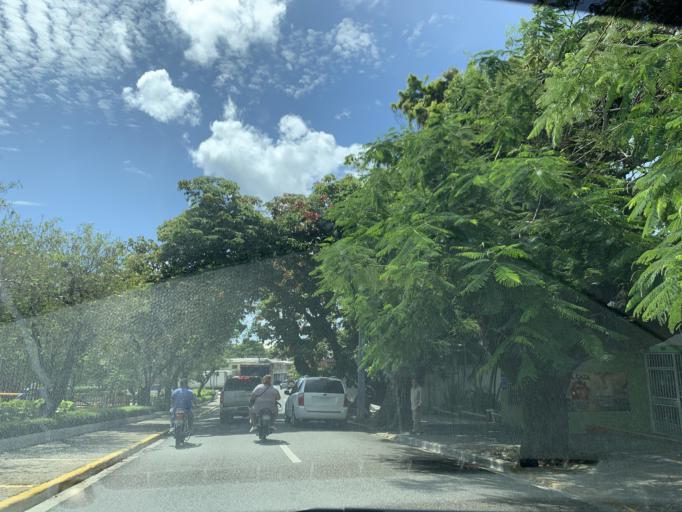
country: DO
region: Puerto Plata
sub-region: Puerto Plata
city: Puerto Plata
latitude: 19.7941
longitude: -70.6851
